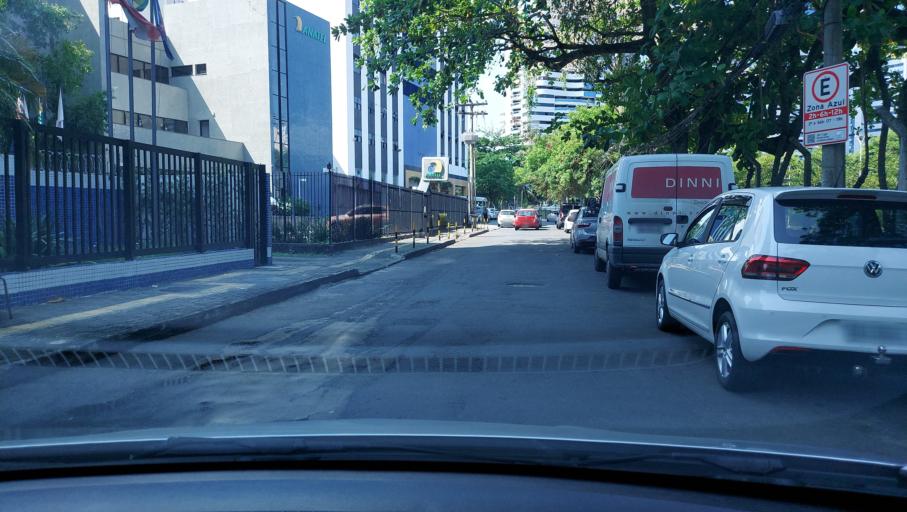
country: BR
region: Bahia
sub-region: Salvador
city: Salvador
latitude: -12.9827
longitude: -38.4531
